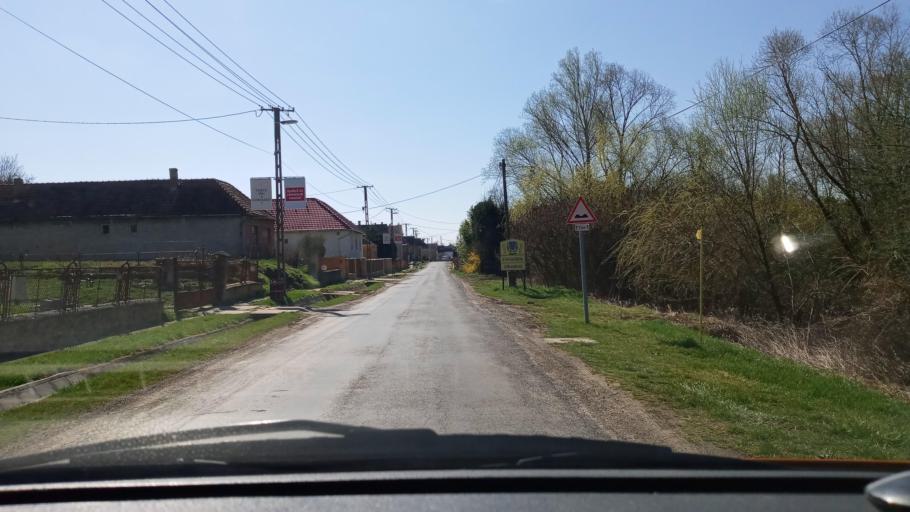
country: HU
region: Baranya
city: Kozarmisleny
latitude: 46.0630
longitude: 18.3733
